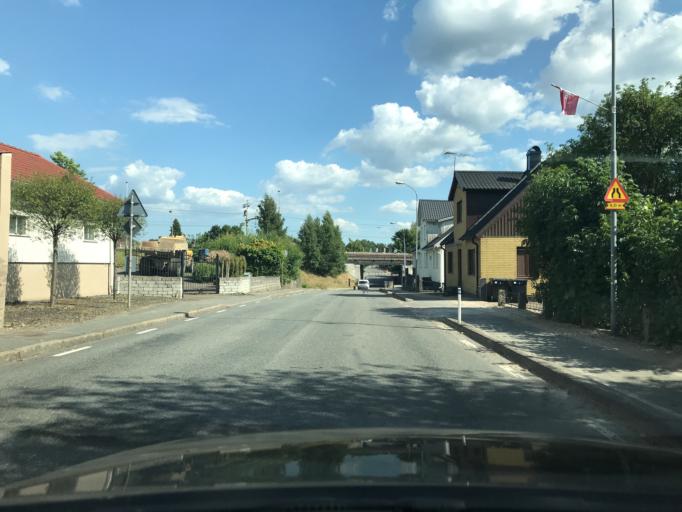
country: SE
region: Skane
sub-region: Hassleholms Kommun
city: Hastveda
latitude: 56.2861
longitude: 13.9317
